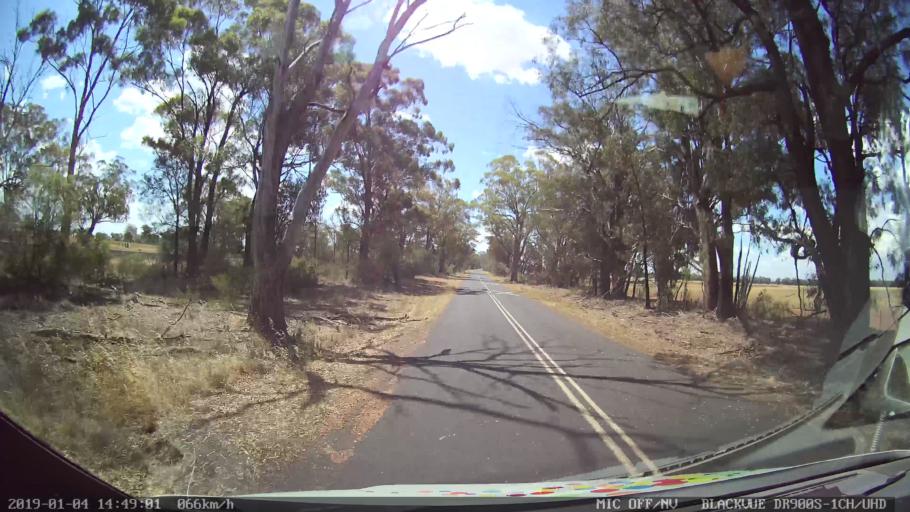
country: AU
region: New South Wales
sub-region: Dubbo Municipality
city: Dubbo
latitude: -32.0536
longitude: 148.6653
